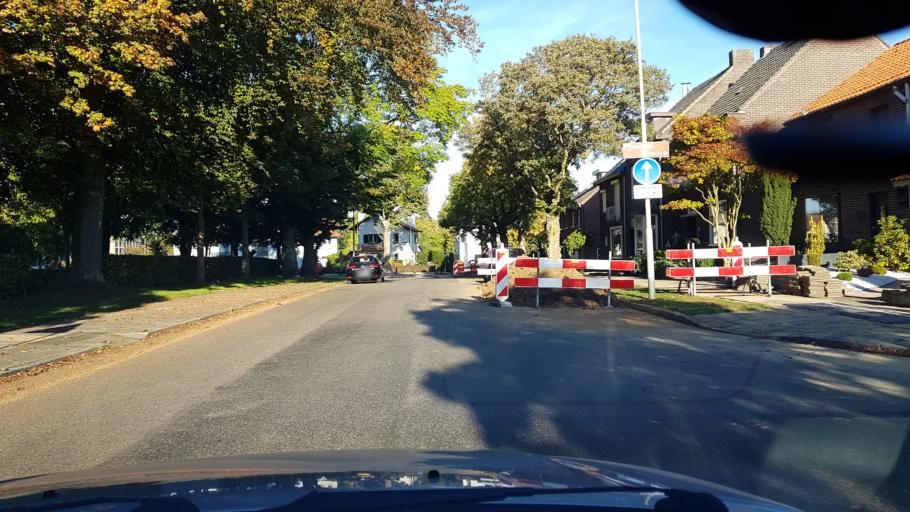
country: NL
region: Limburg
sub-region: Gemeente Schinnen
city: Puth
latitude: 50.9678
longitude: 5.8373
